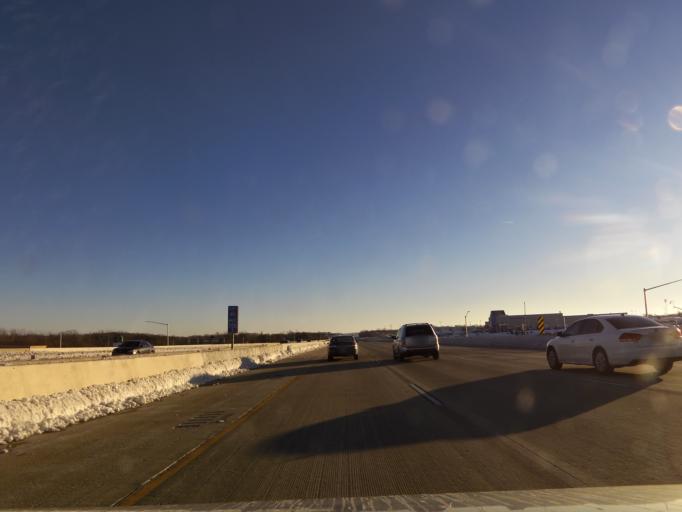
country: US
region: Wisconsin
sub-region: Kenosha County
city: Pleasant Prairie
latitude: 42.5683
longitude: -87.9529
